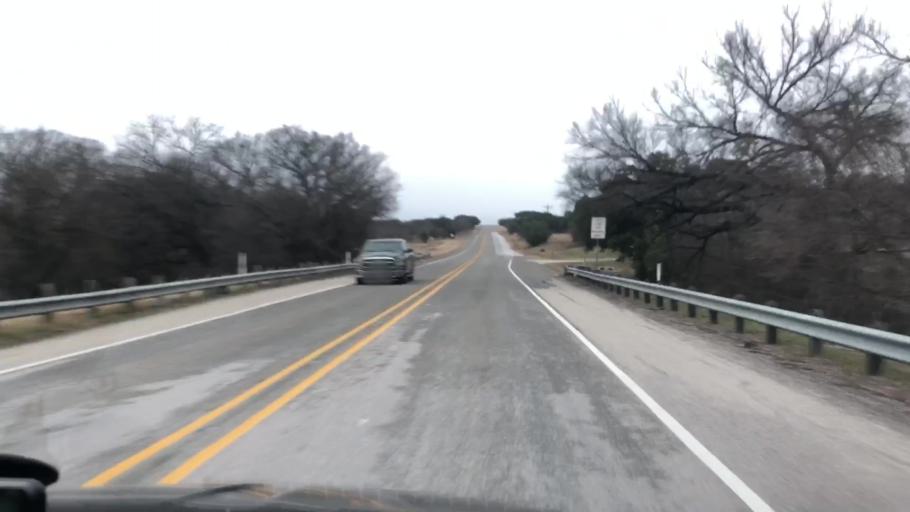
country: US
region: Texas
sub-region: Lampasas County
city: Lampasas
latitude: 31.2687
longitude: -98.1742
